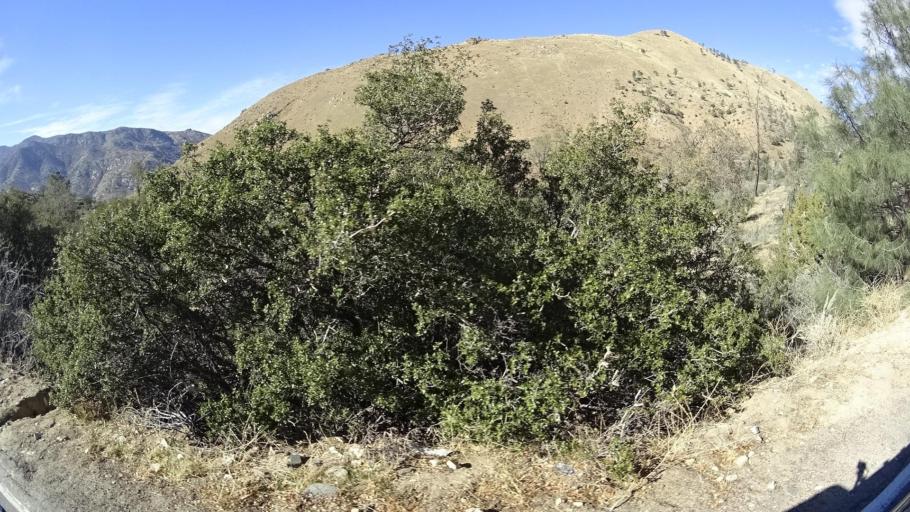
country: US
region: California
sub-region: Kern County
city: Bodfish
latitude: 35.5581
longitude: -118.5079
